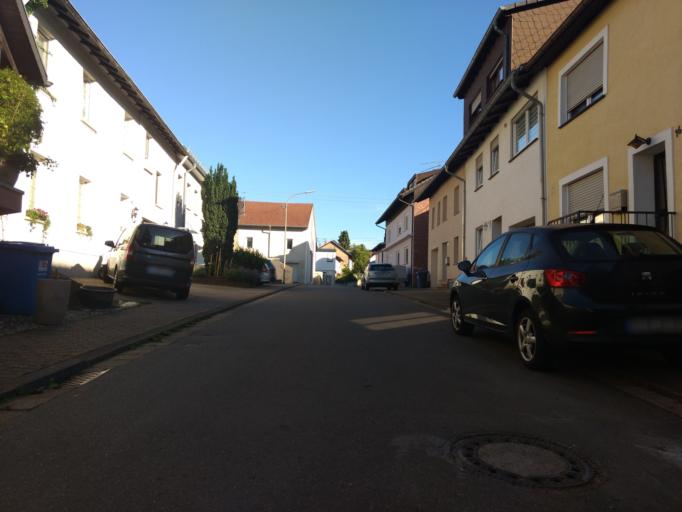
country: DE
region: Saarland
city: Merzig
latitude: 49.4046
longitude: 6.6482
